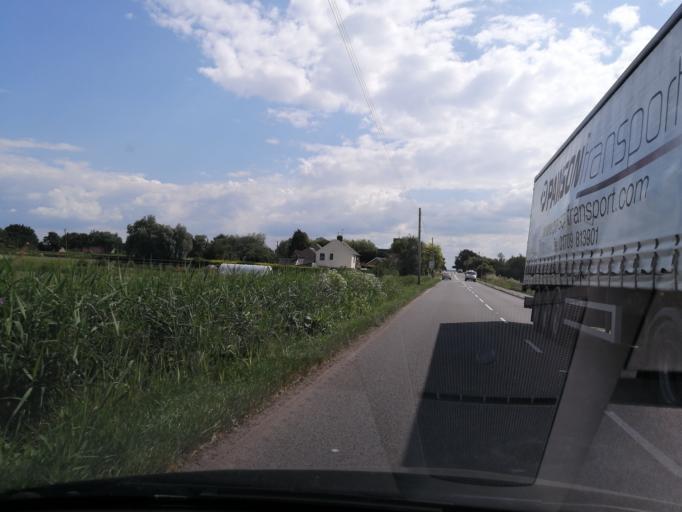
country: GB
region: England
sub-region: Cambridgeshire
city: Ramsey
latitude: 52.4715
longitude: -0.1532
